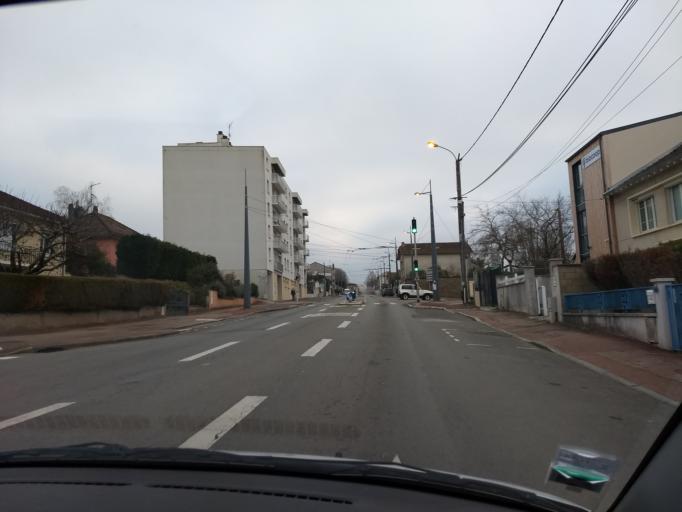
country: FR
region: Limousin
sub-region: Departement de la Haute-Vienne
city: Isle
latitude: 45.8234
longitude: 1.2220
